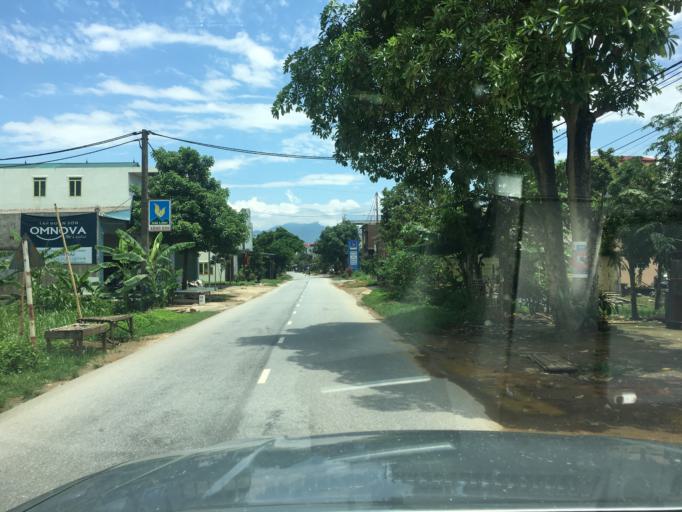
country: VN
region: Yen Bai
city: Son Thinh
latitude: 21.6427
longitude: 104.5005
